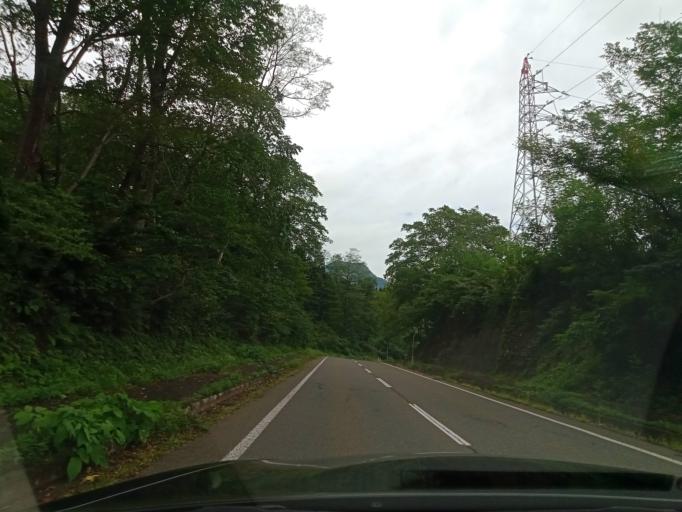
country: JP
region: Niigata
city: Arai
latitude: 36.8772
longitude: 138.2016
